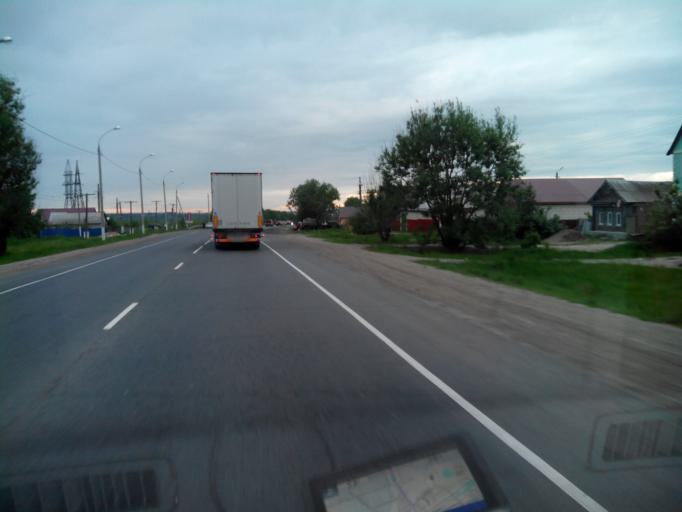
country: RU
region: Penza
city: Chemodanovka
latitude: 53.2172
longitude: 45.2750
